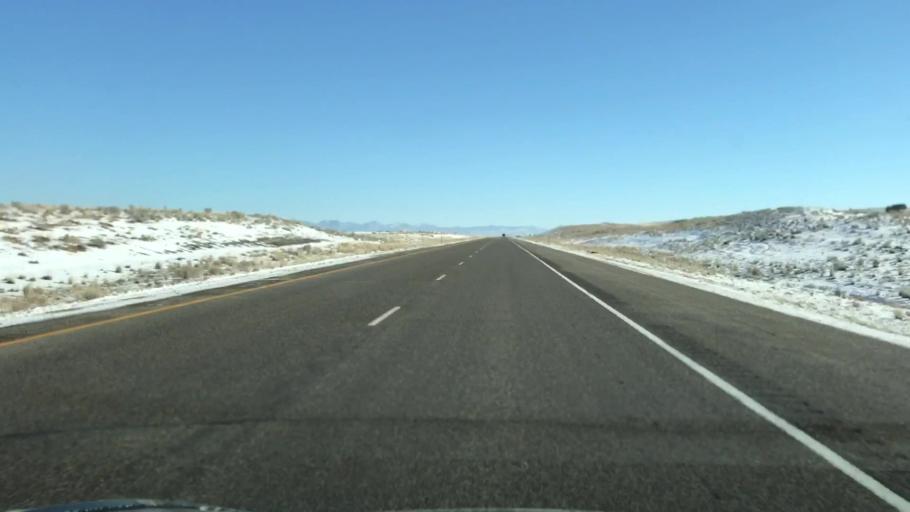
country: US
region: Colorado
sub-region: Mesa County
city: Loma
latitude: 39.2234
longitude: -108.9397
